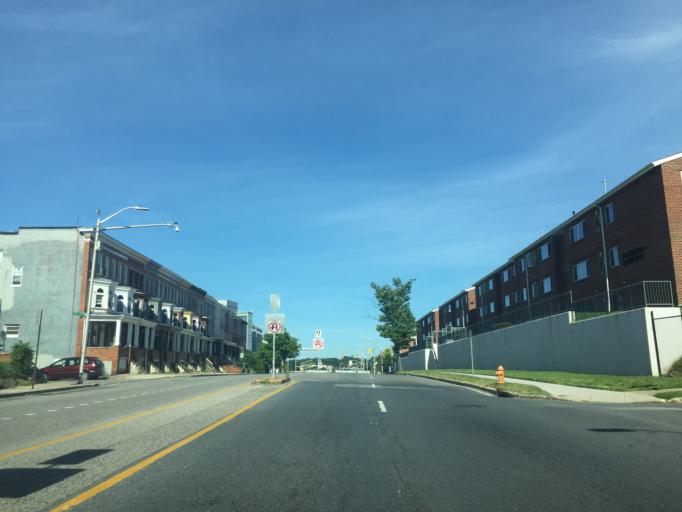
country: US
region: Maryland
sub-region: City of Baltimore
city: Baltimore
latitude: 39.3096
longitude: -76.6553
